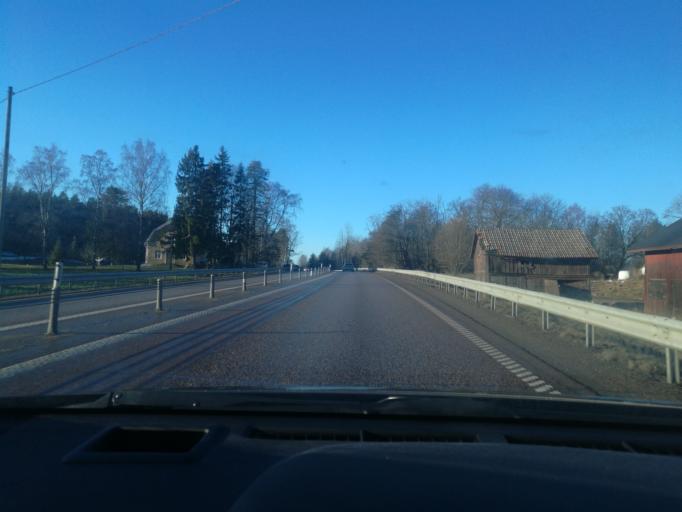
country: SE
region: Soedermanland
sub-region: Eskilstuna Kommun
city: Kvicksund
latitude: 59.4126
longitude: 16.2220
